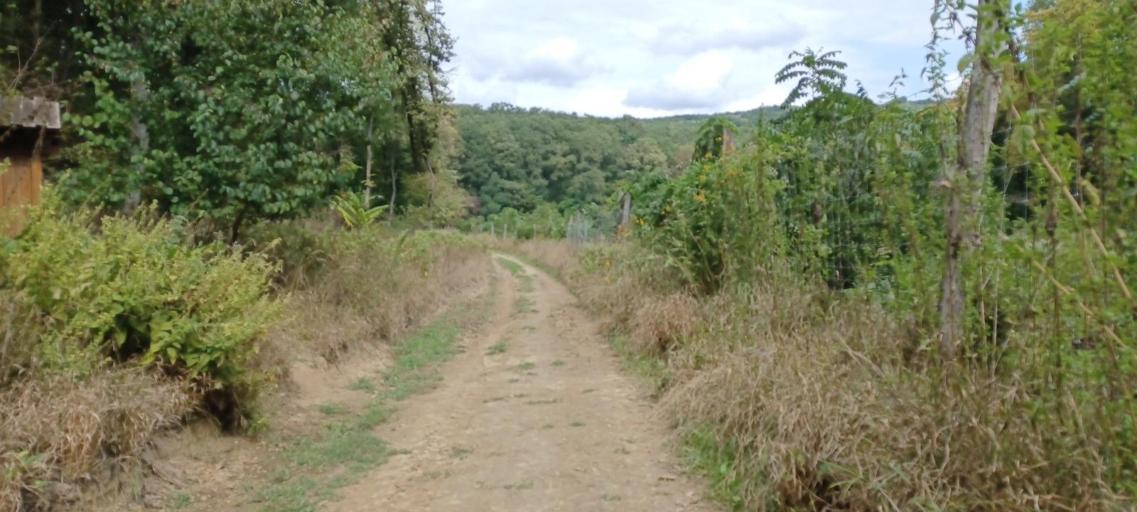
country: HU
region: Tolna
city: Szentgalpuszta
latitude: 46.3301
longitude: 18.6187
